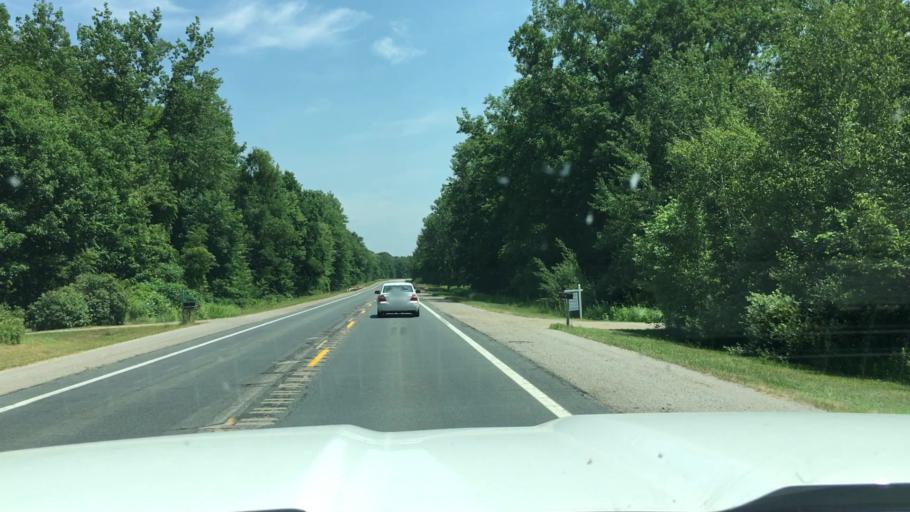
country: US
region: Michigan
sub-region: Clinton County
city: Ovid
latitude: 43.1842
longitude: -84.3368
